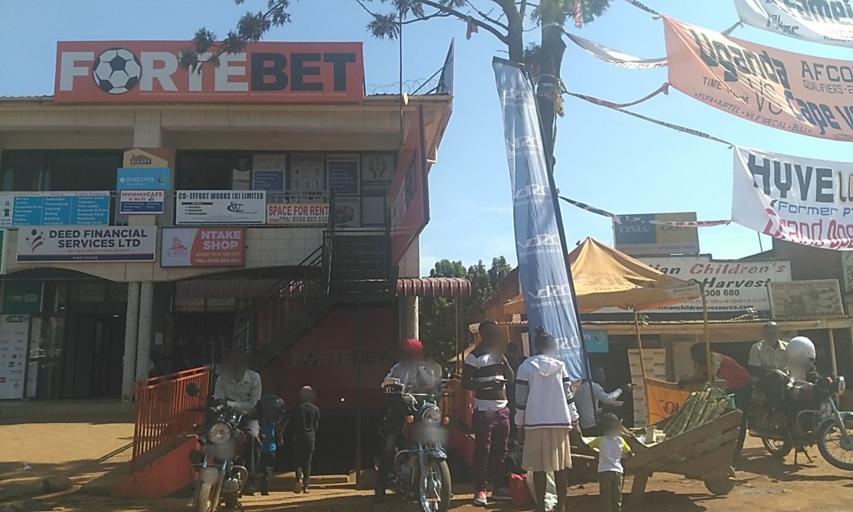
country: UG
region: Central Region
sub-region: Wakiso District
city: Kireka
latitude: 0.3465
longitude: 32.6489
